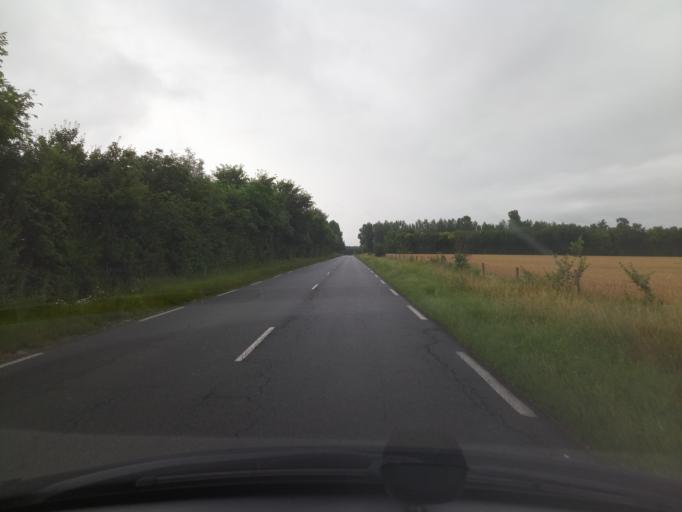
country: FR
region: Poitou-Charentes
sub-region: Departement de la Charente-Maritime
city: Courcon
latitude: 46.1696
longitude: -0.8385
